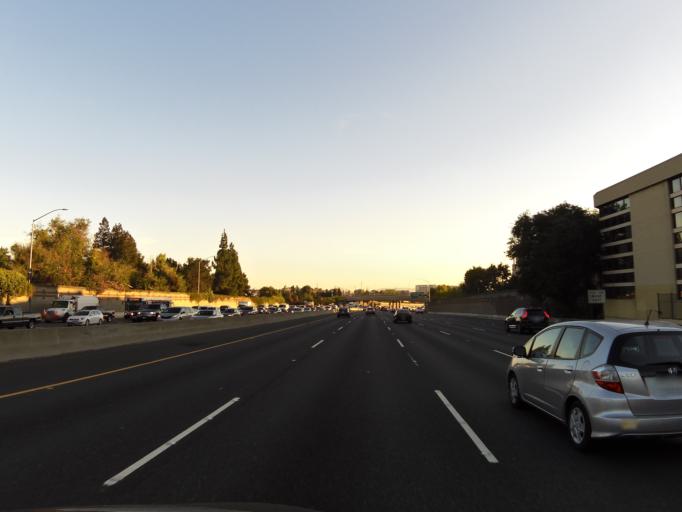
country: US
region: California
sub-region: Contra Costa County
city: Walnut Creek
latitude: 37.9125
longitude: -122.0671
